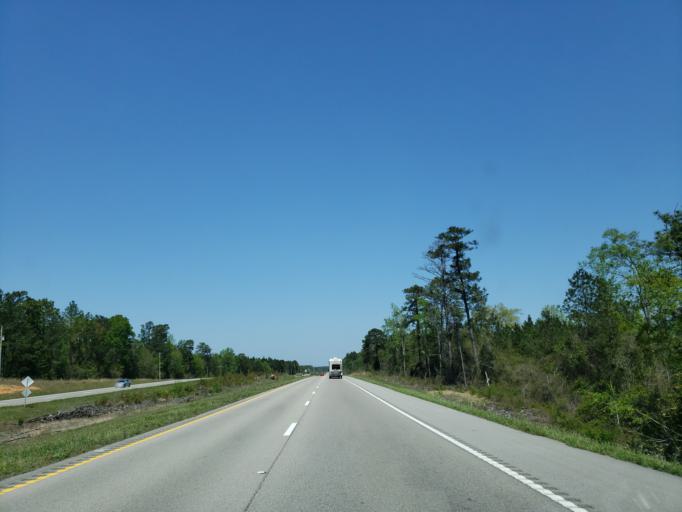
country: US
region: Mississippi
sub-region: Stone County
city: Wiggins
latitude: 30.9579
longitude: -89.1906
